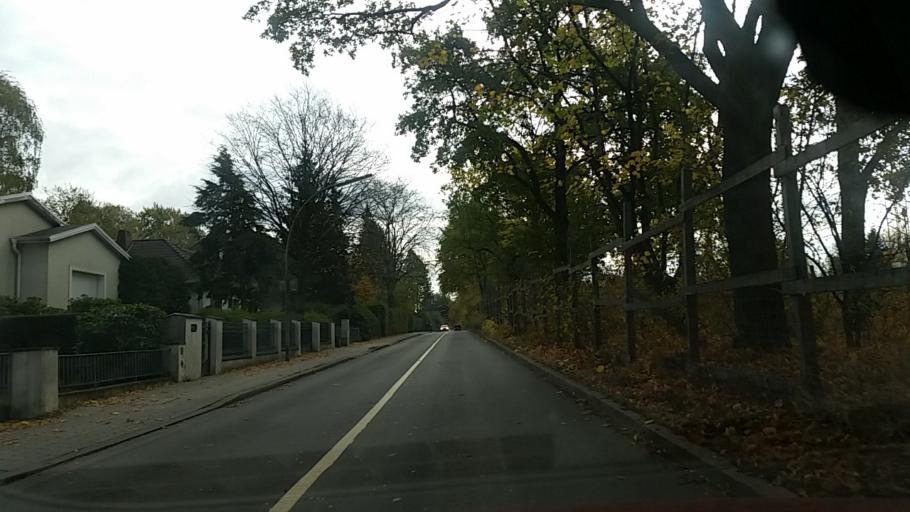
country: DE
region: Hamburg
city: Marienthal
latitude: 53.5657
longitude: 10.0649
